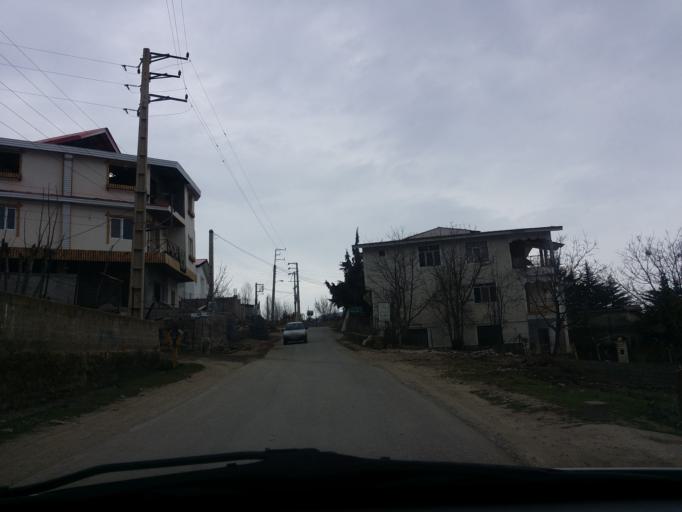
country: IR
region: Mazandaran
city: `Abbasabad
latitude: 36.5322
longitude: 51.1610
